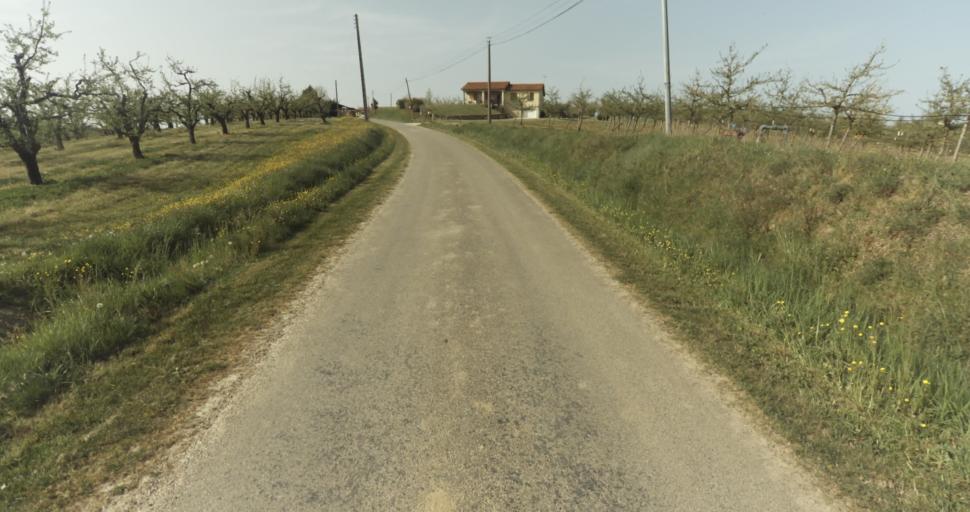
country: FR
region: Midi-Pyrenees
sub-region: Departement du Tarn-et-Garonne
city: Lafrancaise
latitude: 44.1432
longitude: 1.1643
